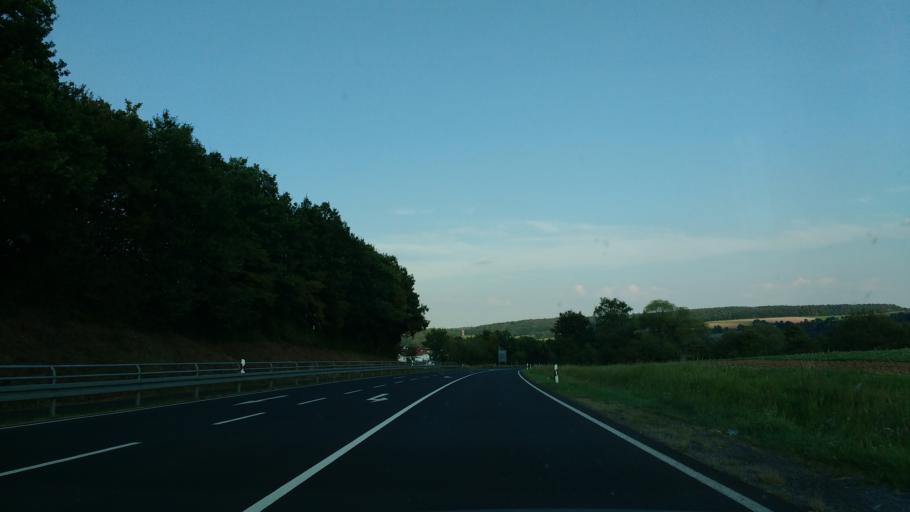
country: DE
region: Bavaria
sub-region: Regierungsbezirk Unterfranken
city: Oberthulba
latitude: 50.1985
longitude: 9.9426
